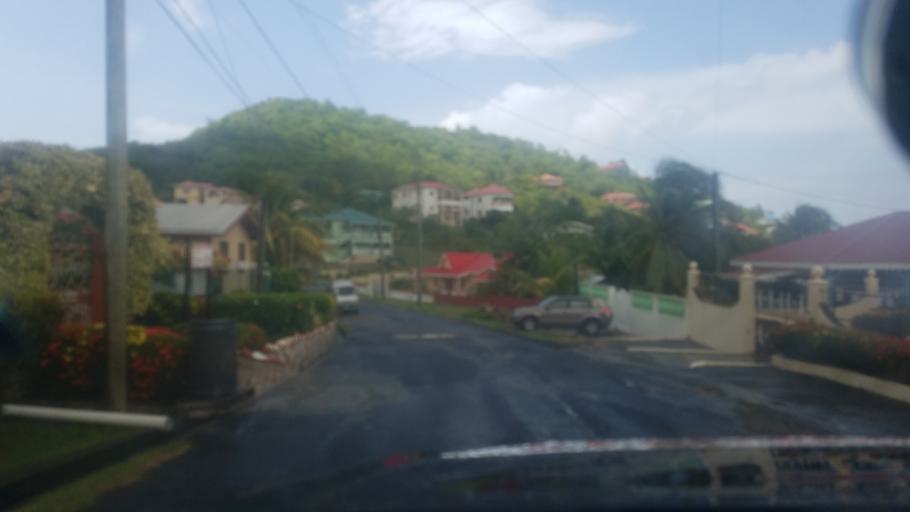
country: LC
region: Laborie Quarter
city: Laborie
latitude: 13.7467
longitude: -60.9680
